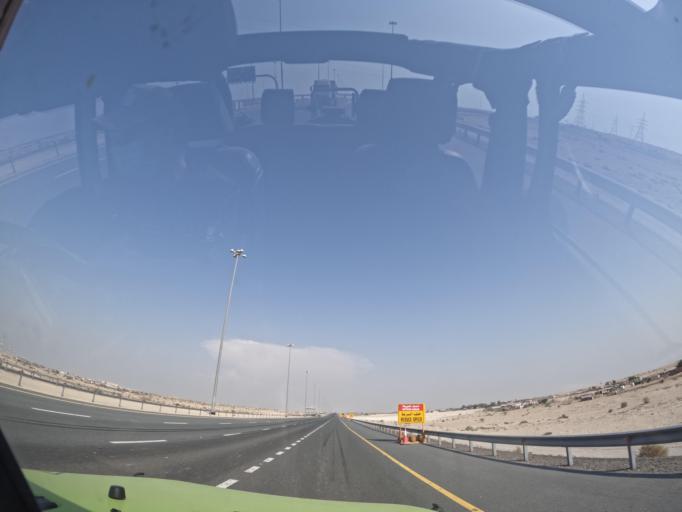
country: AE
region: Abu Dhabi
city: Abu Dhabi
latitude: 24.6775
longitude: 54.8299
